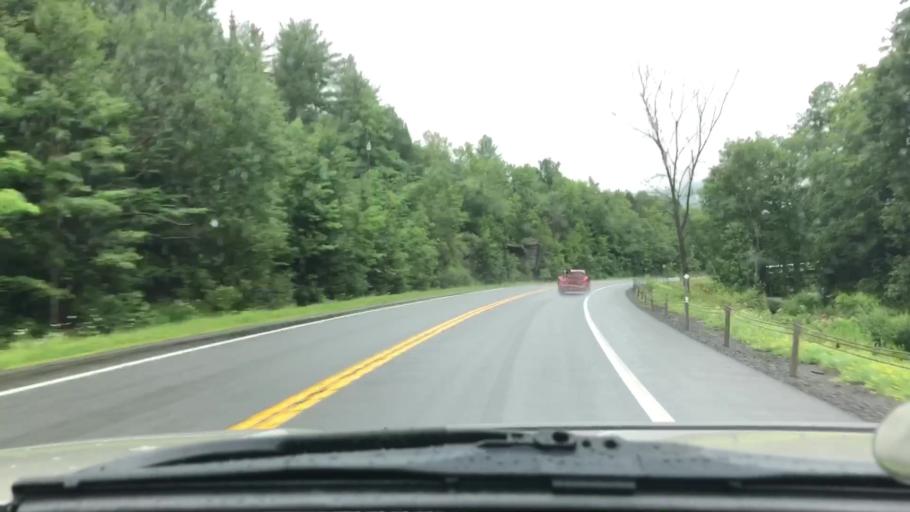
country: US
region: New York
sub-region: Greene County
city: Cairo
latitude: 42.3066
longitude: -74.1940
